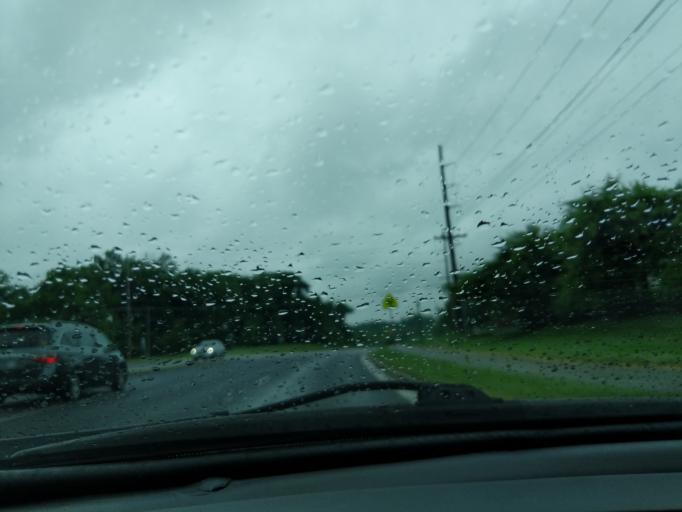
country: US
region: Indiana
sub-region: Hamilton County
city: Noblesville
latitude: 40.0600
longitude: -86.0341
